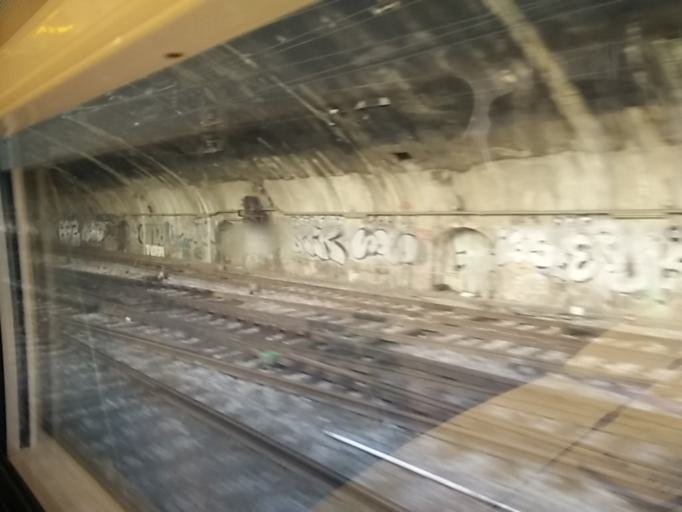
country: FR
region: Ile-de-France
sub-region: Paris
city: Paris
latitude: 48.8821
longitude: 2.3616
